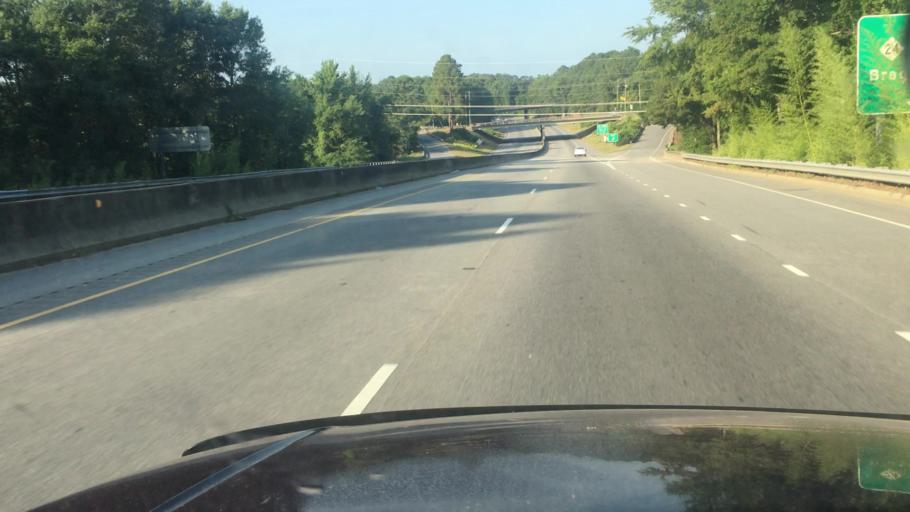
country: US
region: North Carolina
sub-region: Cumberland County
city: Fayetteville
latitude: 35.0647
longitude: -78.8884
